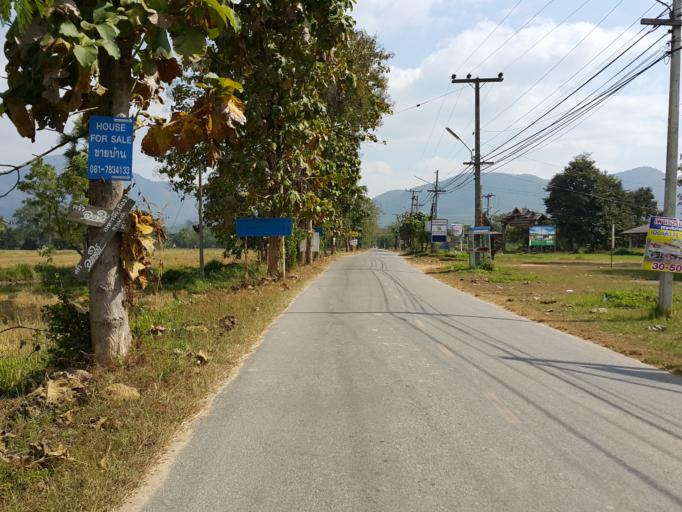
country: TH
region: Chiang Mai
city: Mae On
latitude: 18.7248
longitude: 99.2015
